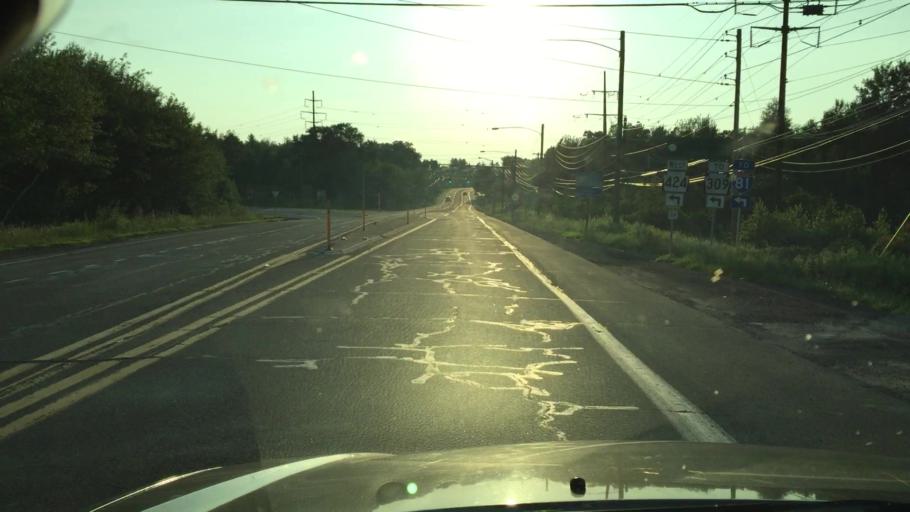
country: US
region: Pennsylvania
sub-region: Luzerne County
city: Hazleton
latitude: 40.9400
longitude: -75.9444
